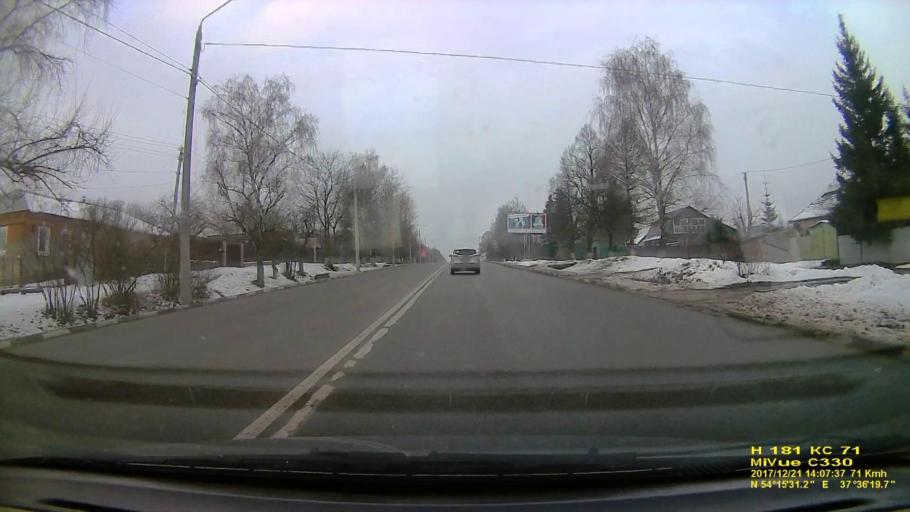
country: RU
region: Tula
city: Gorelki
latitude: 54.2589
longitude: 37.6053
